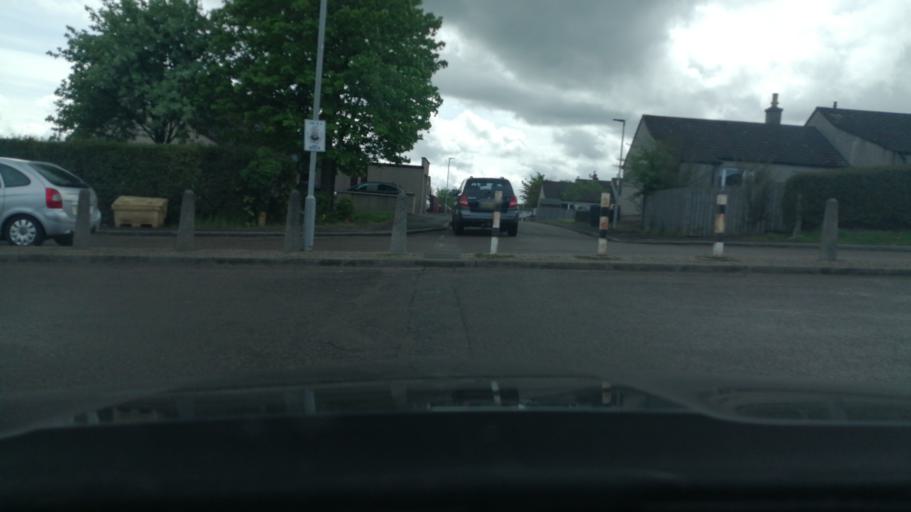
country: GB
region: Scotland
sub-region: Moray
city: Keith
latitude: 57.5405
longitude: -2.9637
